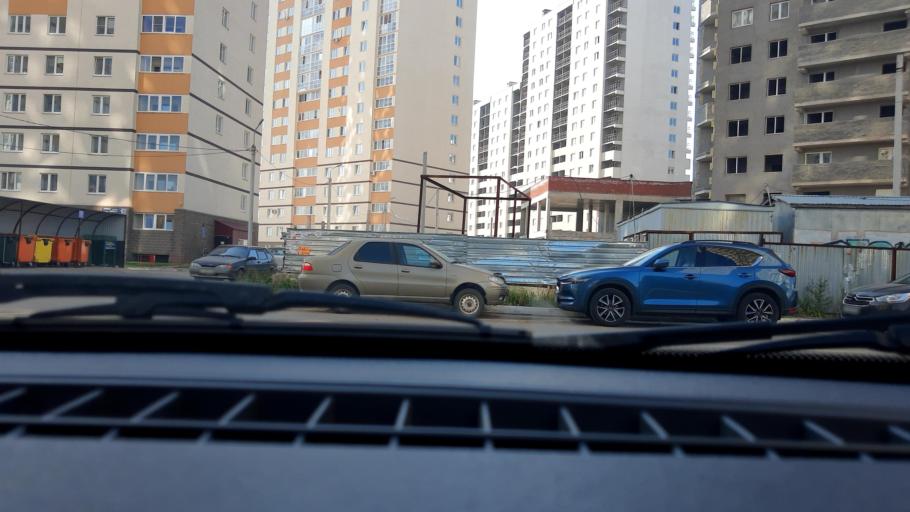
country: RU
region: Bashkortostan
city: Mikhaylovka
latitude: 54.7902
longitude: 55.8707
